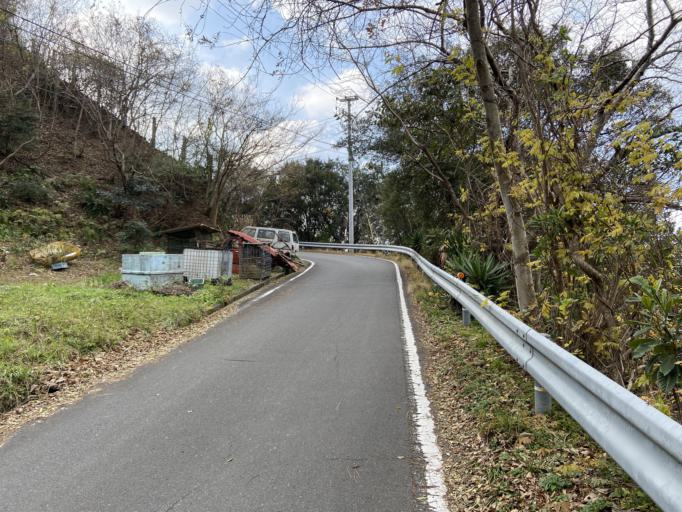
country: JP
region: Ehime
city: Uwajima
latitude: 33.2611
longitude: 132.5420
